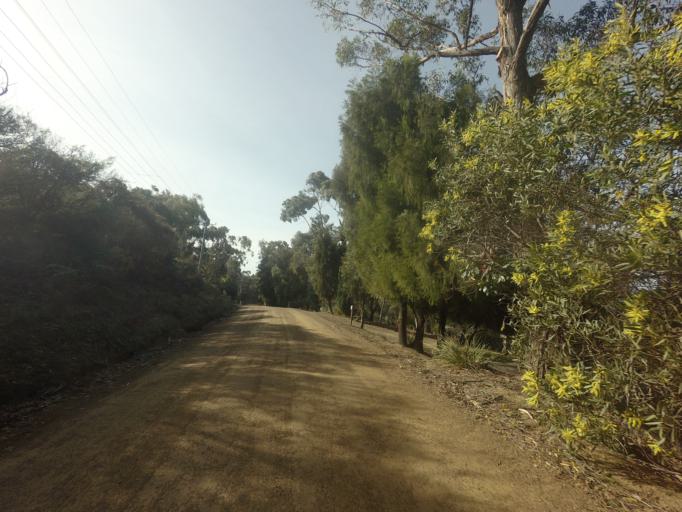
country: AU
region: Tasmania
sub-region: Kingborough
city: Kettering
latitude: -43.1202
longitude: 147.2638
